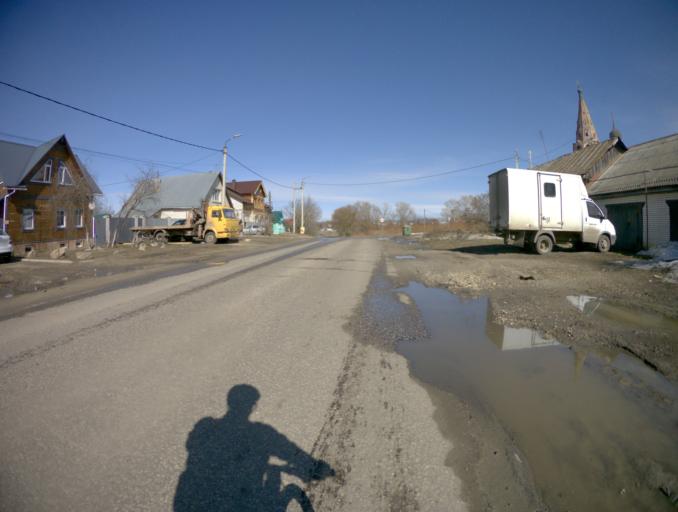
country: RU
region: Vladimir
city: Suzdal'
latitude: 56.4339
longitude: 40.4270
